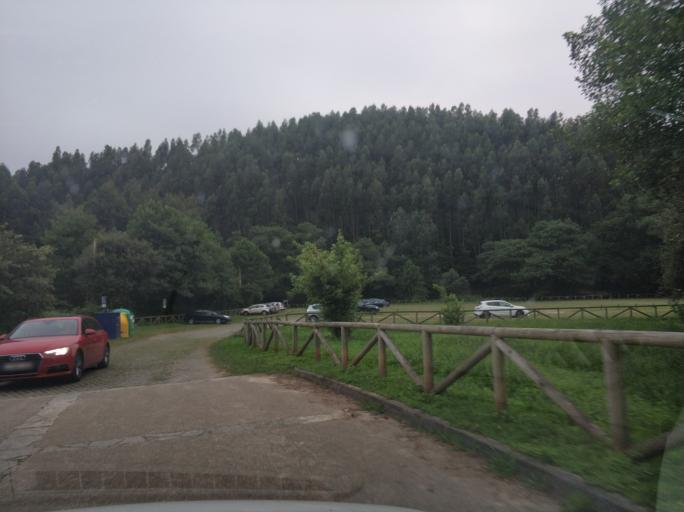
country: ES
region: Asturias
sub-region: Province of Asturias
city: Cudillero
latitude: 43.5598
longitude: -6.1881
